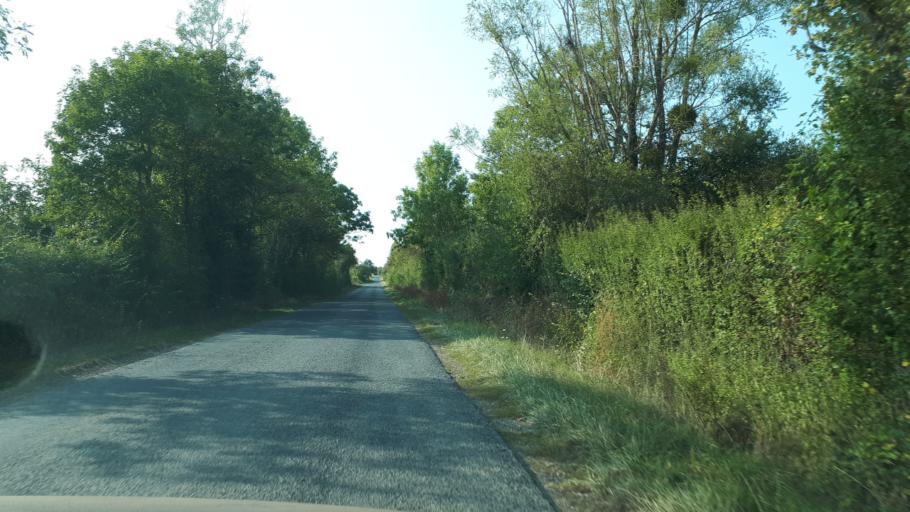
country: FR
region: Centre
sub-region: Departement du Cher
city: Menetou-Salon
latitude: 47.2233
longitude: 2.5289
